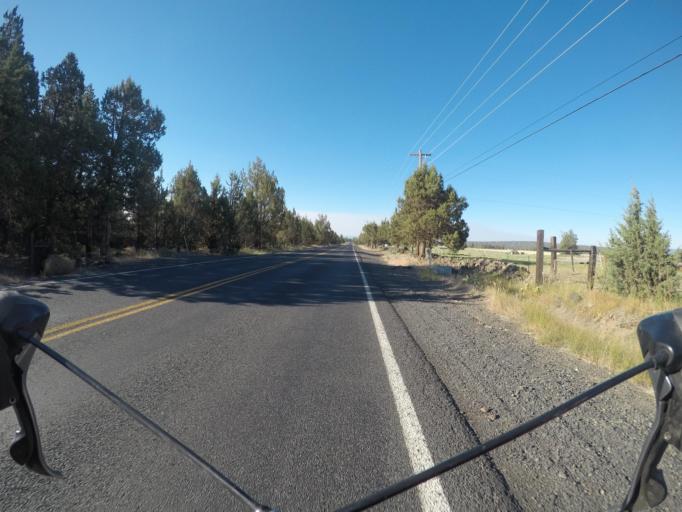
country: US
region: Oregon
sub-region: Deschutes County
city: Redmond
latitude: 44.2071
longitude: -121.2436
